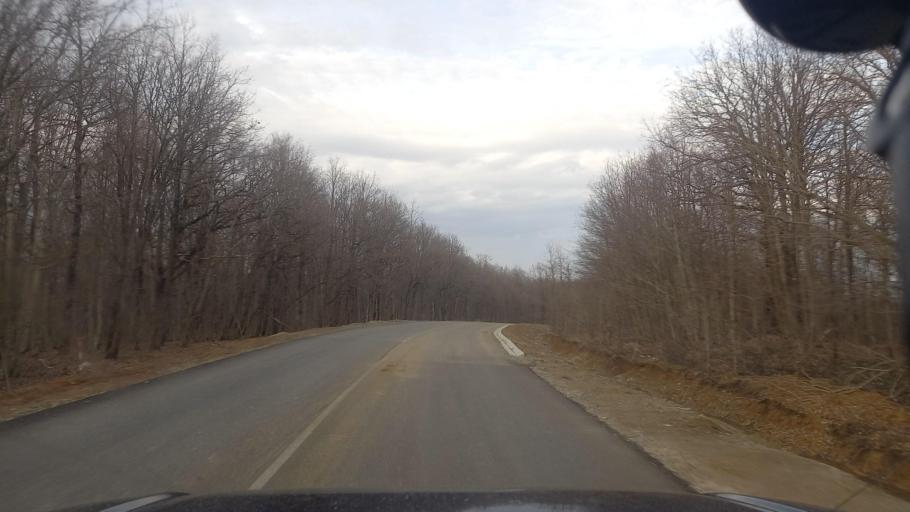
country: RU
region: Krasnodarskiy
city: Goryachiy Klyuch
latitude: 44.7067
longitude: 39.0046
